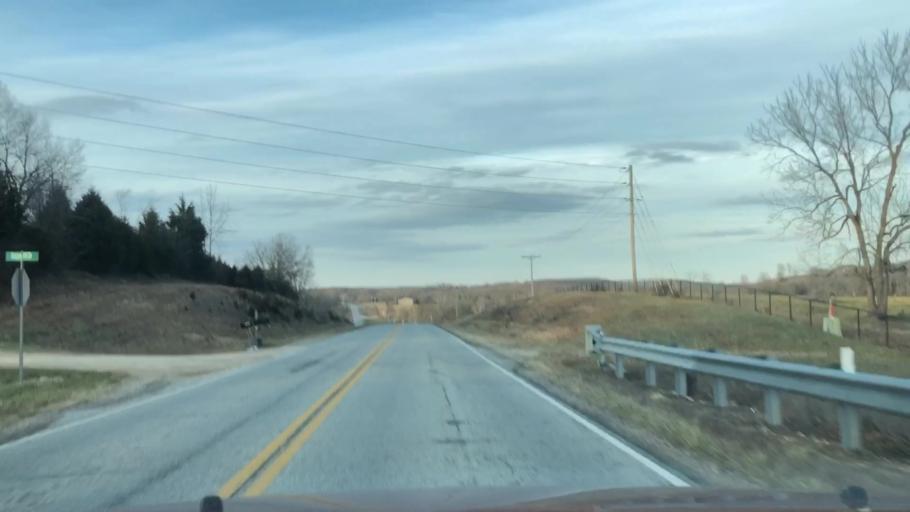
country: US
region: Missouri
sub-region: Webster County
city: Marshfield
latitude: 37.2416
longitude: -92.8799
